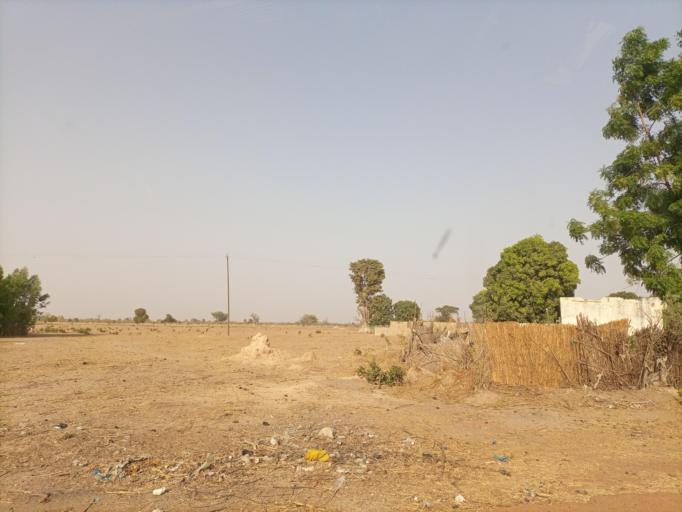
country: SN
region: Fatick
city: Passi
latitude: 14.0370
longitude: -16.3175
